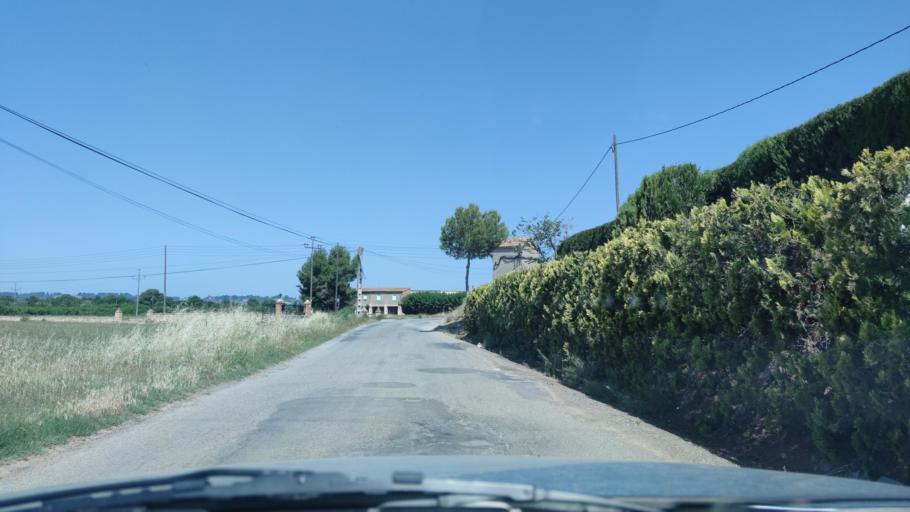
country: ES
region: Catalonia
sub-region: Provincia de Lleida
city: Alpicat
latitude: 41.6495
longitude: 0.5809
